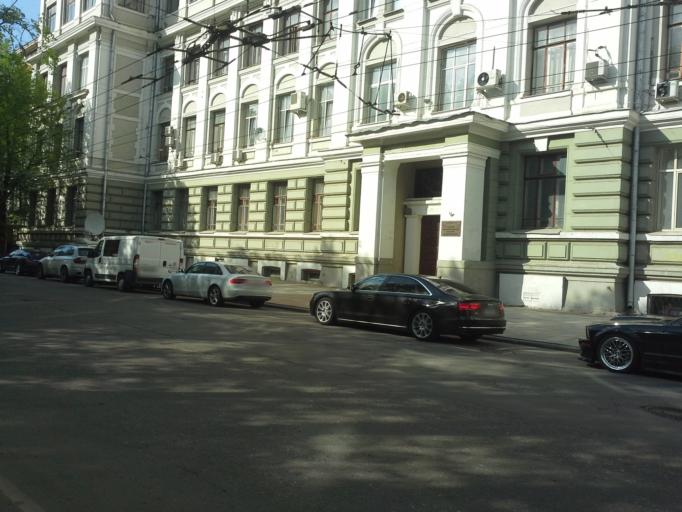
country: RU
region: Moscow
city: Mar'ina Roshcha
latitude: 55.7782
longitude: 37.5947
